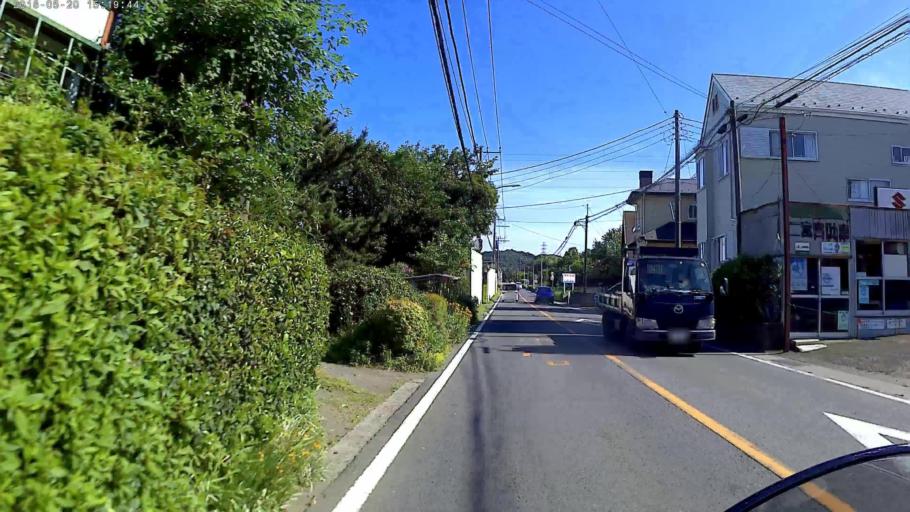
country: JP
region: Kanagawa
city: Oiso
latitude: 35.3399
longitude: 139.2926
